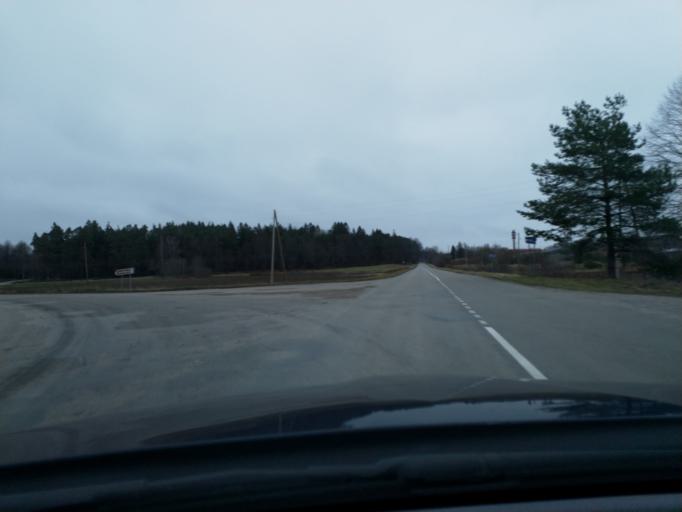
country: LV
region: Ventspils Rajons
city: Piltene
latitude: 57.1180
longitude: 21.8116
